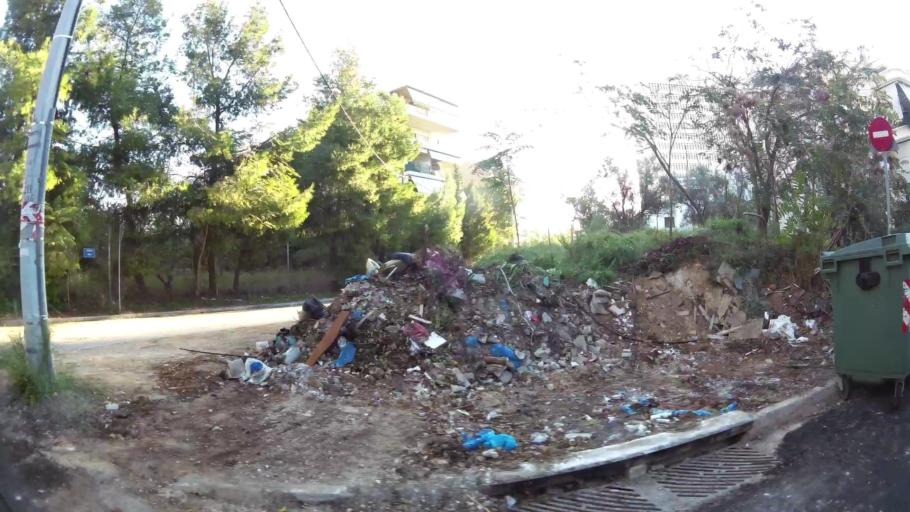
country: GR
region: Attica
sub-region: Nomarchia Athinas
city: Marousi
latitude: 38.0465
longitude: 23.8022
